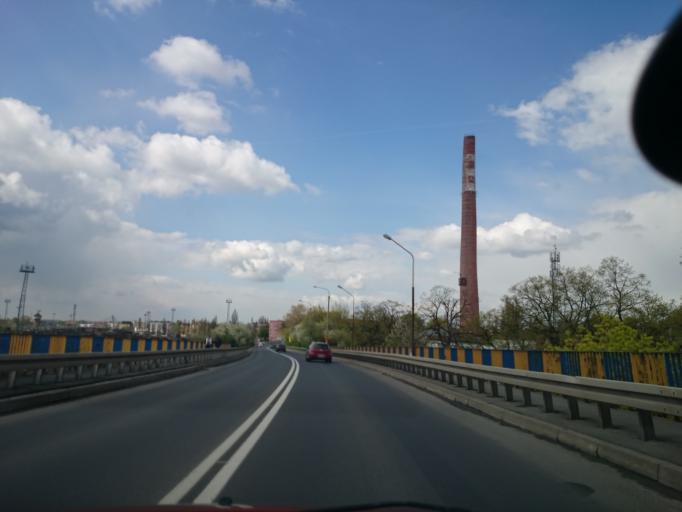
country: PL
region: Opole Voivodeship
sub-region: Powiat opolski
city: Opole
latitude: 50.6577
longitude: 17.9469
